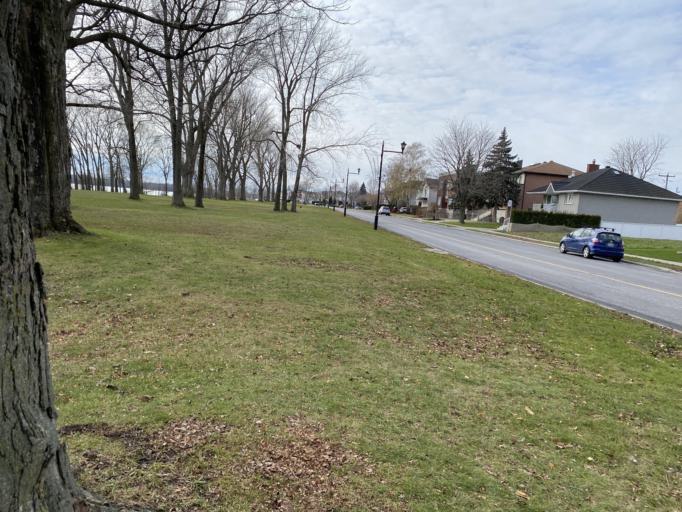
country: CA
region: Quebec
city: Saint-Raymond
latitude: 45.4196
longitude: -73.6046
